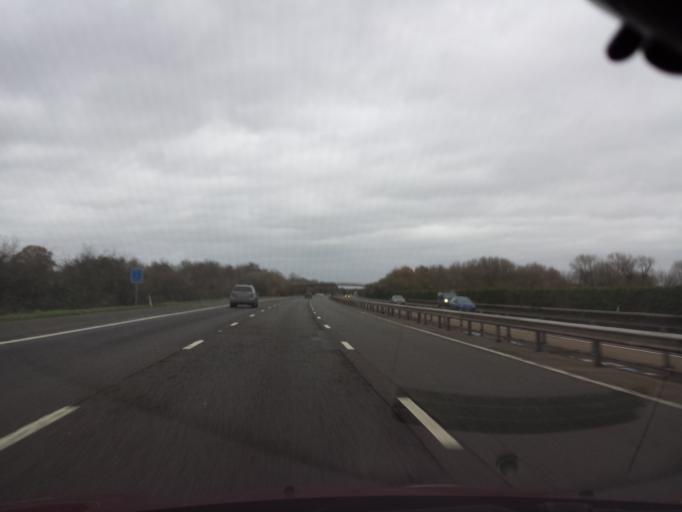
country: GB
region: England
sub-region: Surrey
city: Shepperton
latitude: 51.4010
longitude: -0.4505
